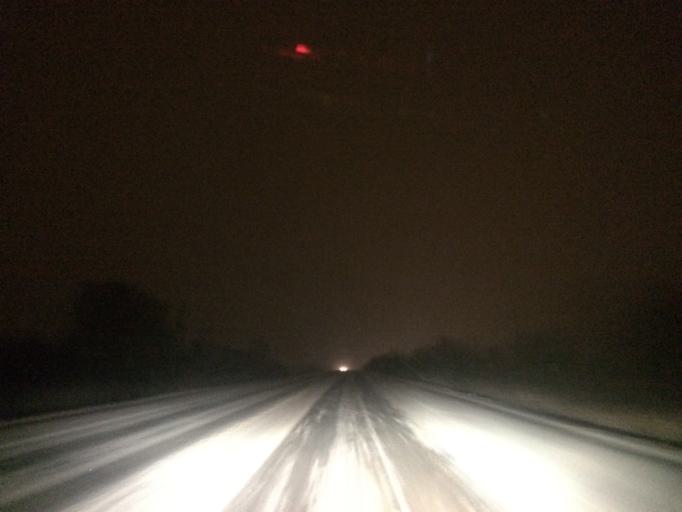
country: RU
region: Tula
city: Kosaya Gora
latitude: 54.1566
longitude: 37.4503
